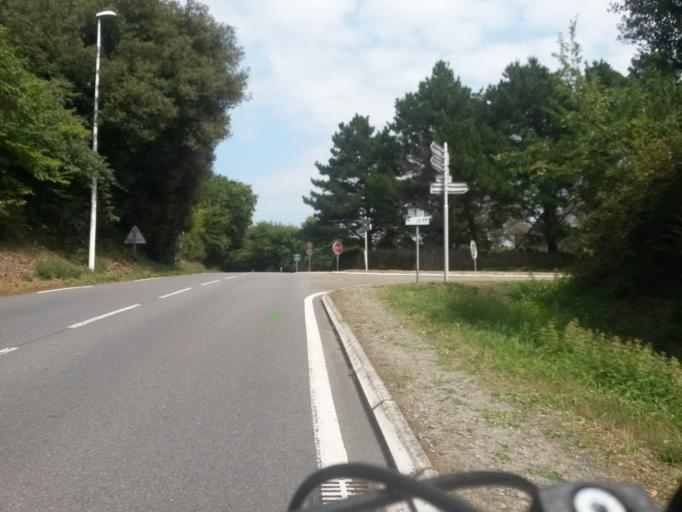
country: FR
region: Pays de la Loire
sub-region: Departement de la Loire-Atlantique
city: Guerande
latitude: 47.3146
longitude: -2.4045
